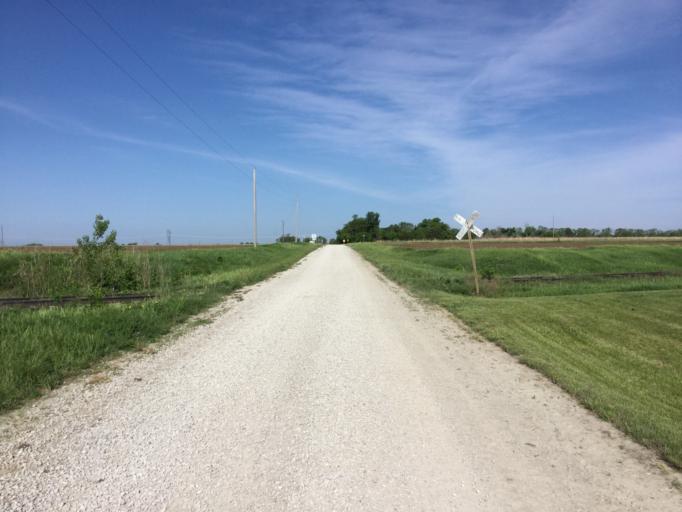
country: US
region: Kansas
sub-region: Coffey County
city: Burlington
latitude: 38.2133
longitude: -95.6447
